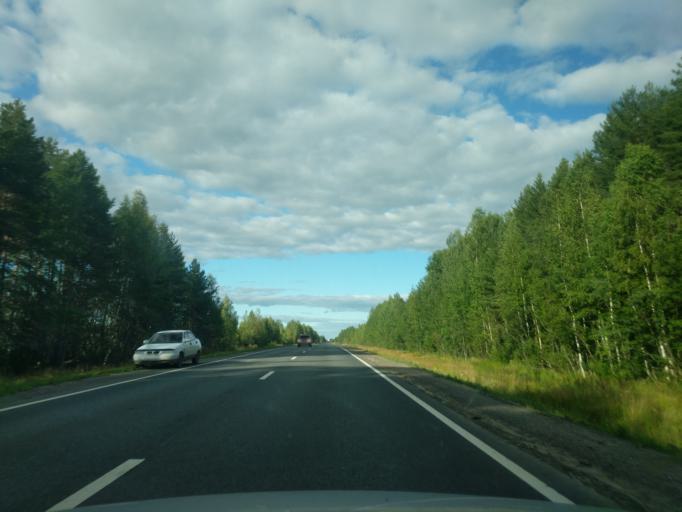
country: RU
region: Kostroma
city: Manturovo
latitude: 58.2267
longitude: 44.6266
